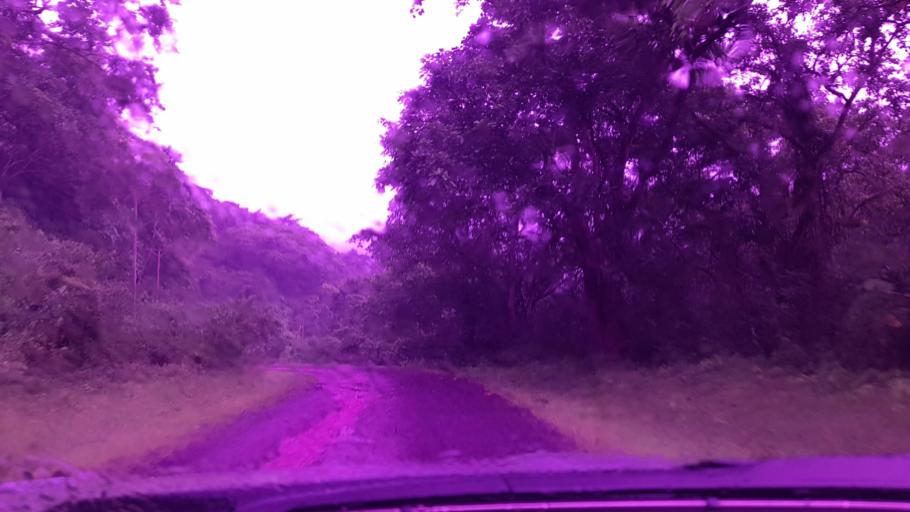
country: ET
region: Oromiya
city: Metu
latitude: 8.4766
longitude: 35.6397
